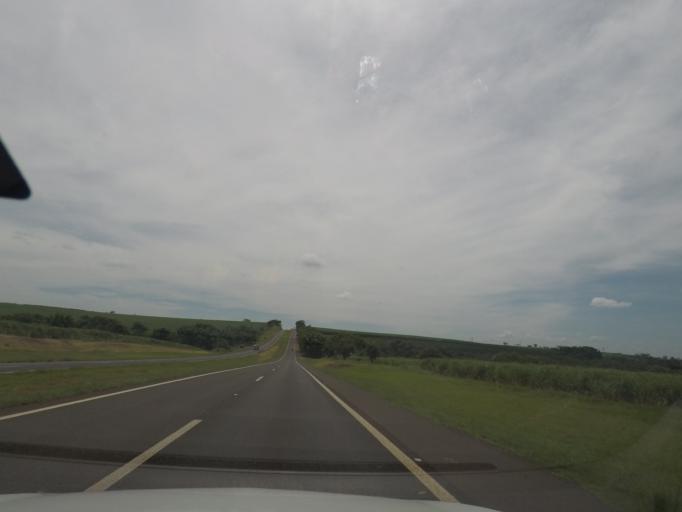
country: BR
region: Sao Paulo
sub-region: Bebedouro
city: Bebedouro
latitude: -21.0310
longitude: -48.4206
